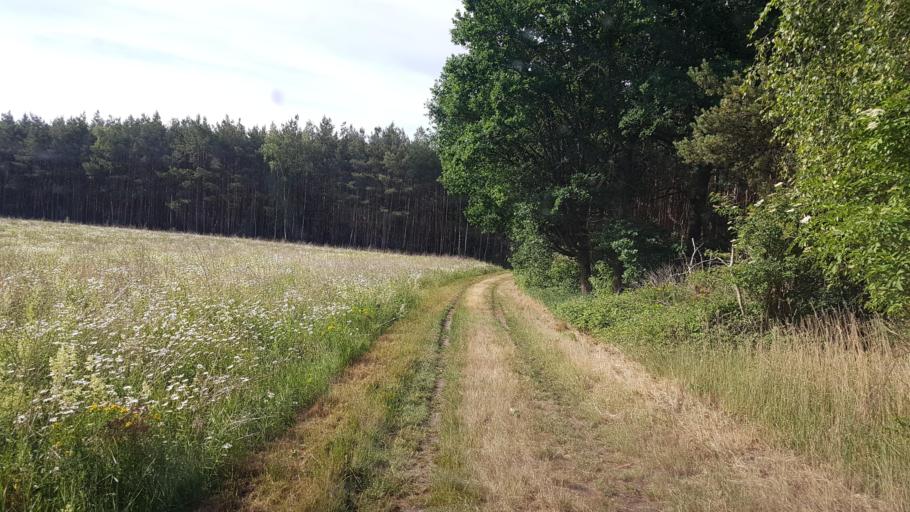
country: DE
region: Brandenburg
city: Plessa
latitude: 51.5305
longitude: 13.6504
